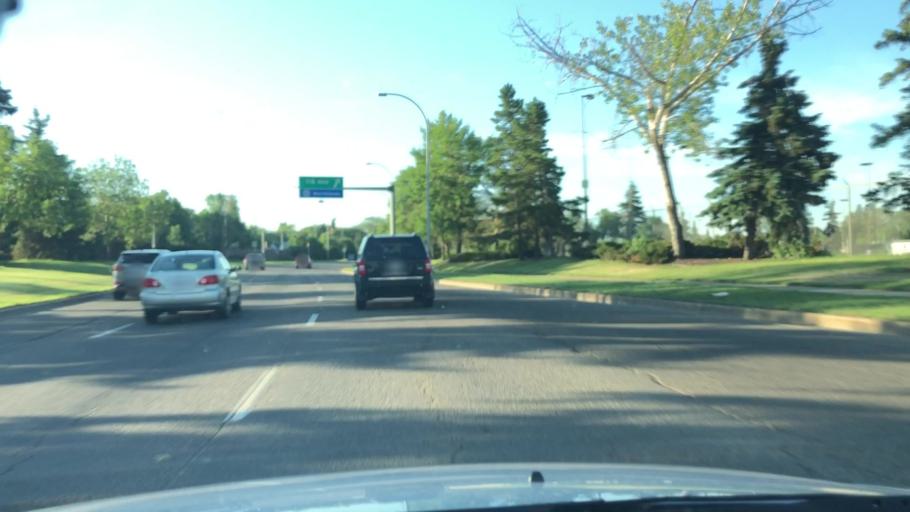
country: CA
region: Alberta
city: Edmonton
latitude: 53.5697
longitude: -113.4531
